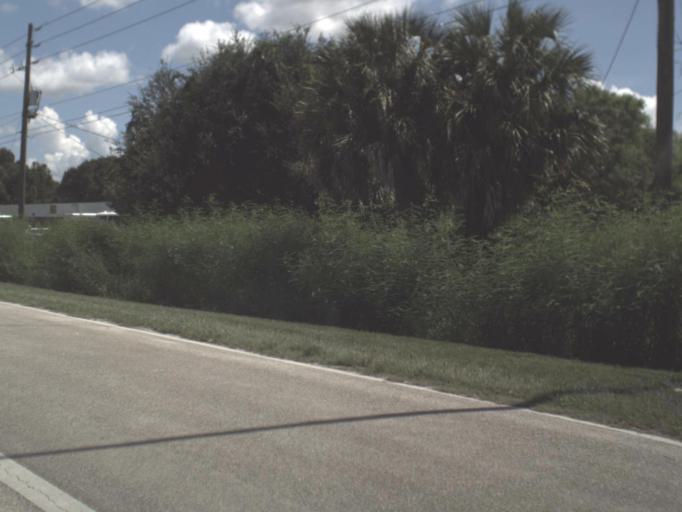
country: US
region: Florida
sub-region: Polk County
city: Combee Settlement
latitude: 28.0478
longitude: -81.8949
